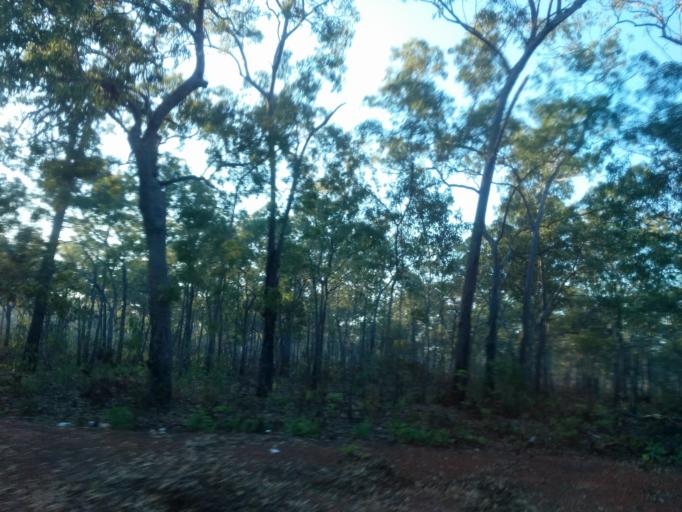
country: AU
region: Northern Territory
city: Alyangula
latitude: -13.8636
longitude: 136.8077
